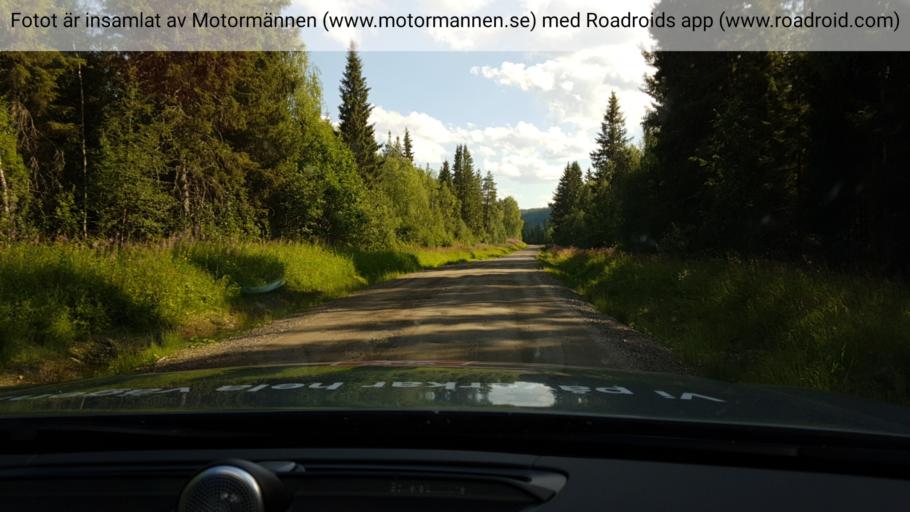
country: SE
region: Jaemtland
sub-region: Stroemsunds Kommun
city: Stroemsund
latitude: 64.0063
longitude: 15.9670
